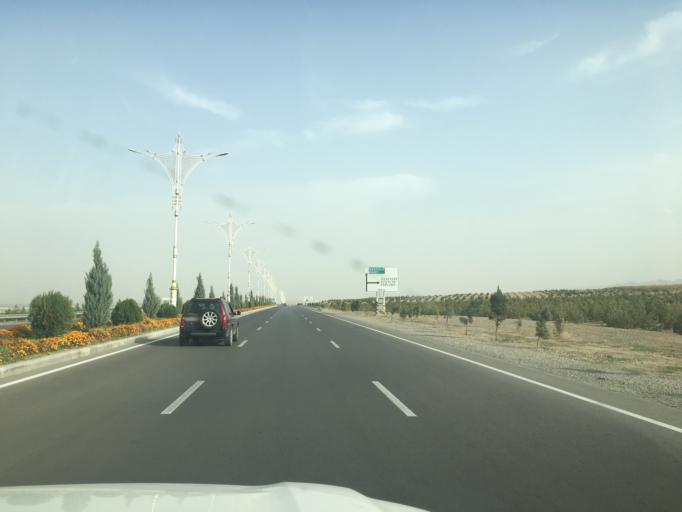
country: TM
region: Ahal
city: Annau
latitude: 37.8772
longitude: 58.4549
